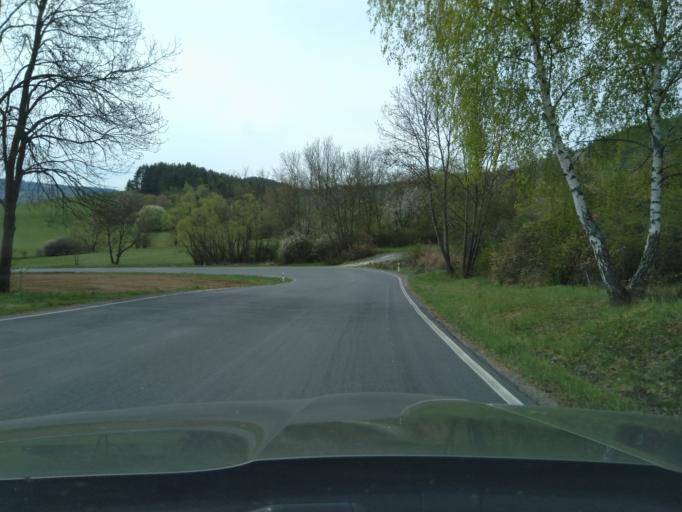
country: CZ
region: Plzensky
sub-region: Okres Klatovy
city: Susice
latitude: 49.2367
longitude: 13.5779
